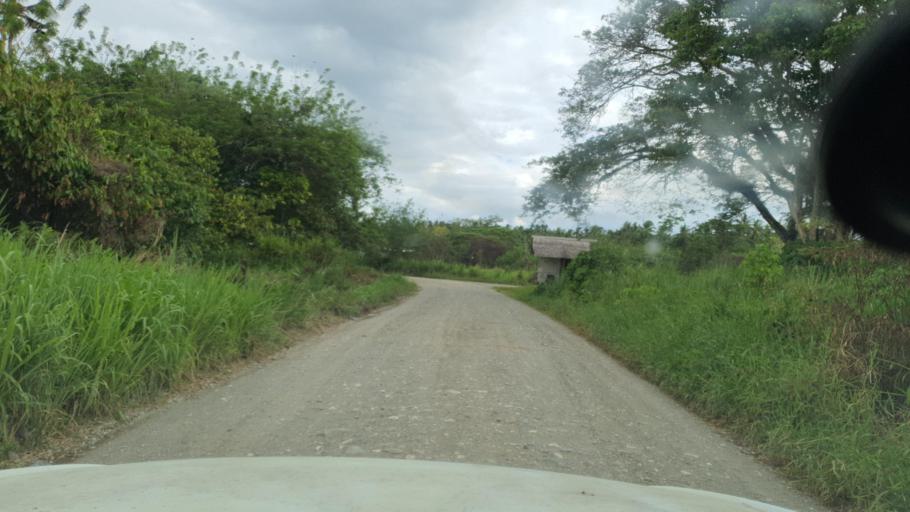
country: SB
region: Guadalcanal
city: Honiara
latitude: -9.4740
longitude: 160.0527
